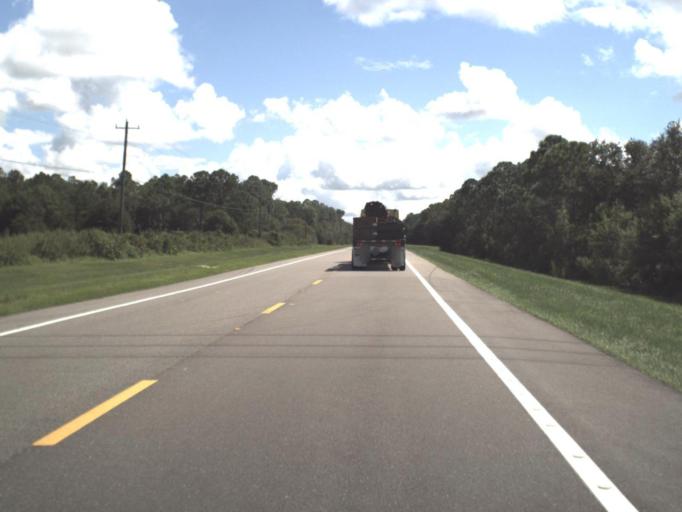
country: US
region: Florida
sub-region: Sarasota County
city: The Meadows
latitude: 27.4159
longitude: -82.3538
